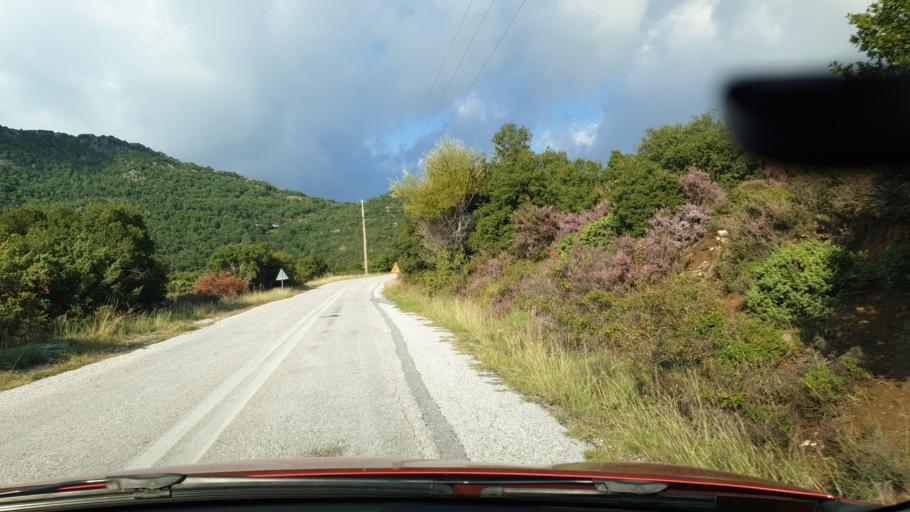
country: GR
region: Central Macedonia
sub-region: Nomos Thessalonikis
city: Peristera
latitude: 40.5233
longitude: 23.1984
